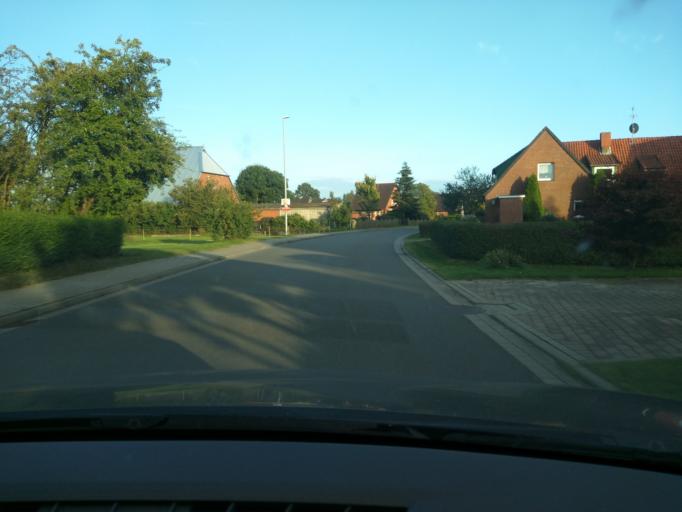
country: DE
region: Lower Saxony
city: Artlenburg
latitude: 53.3857
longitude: 10.4565
